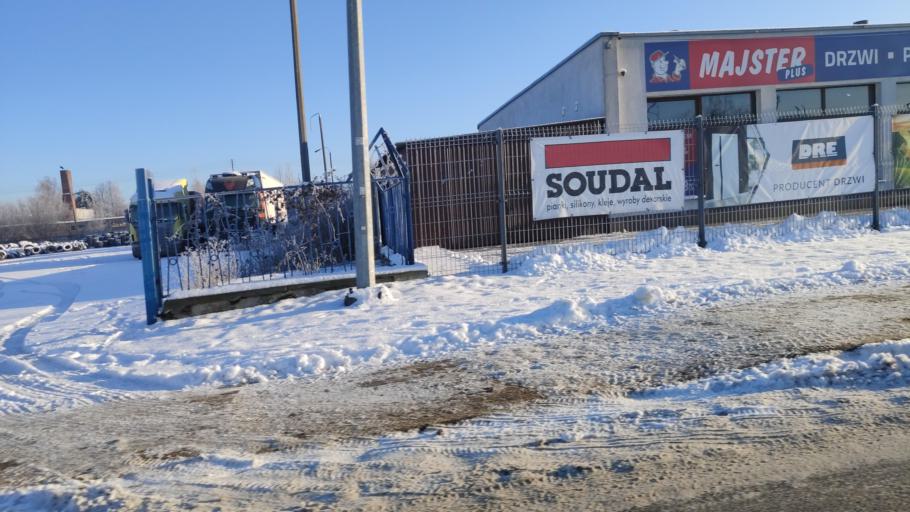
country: PL
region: Kujawsko-Pomorskie
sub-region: Powiat zninski
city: Znin
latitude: 52.8483
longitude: 17.7420
